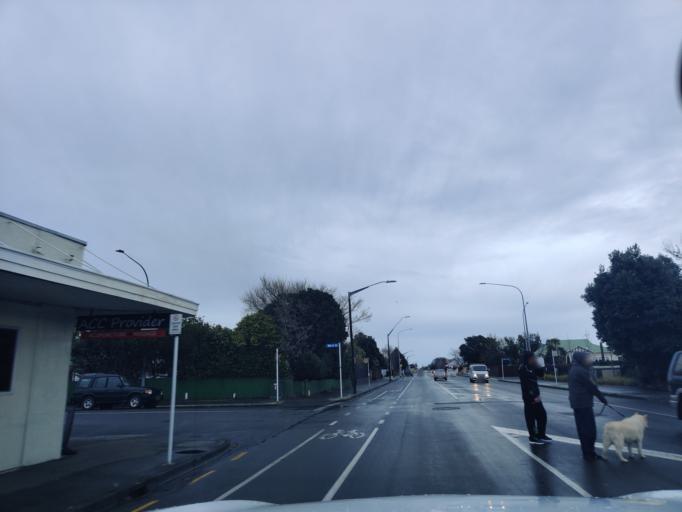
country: NZ
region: Manawatu-Wanganui
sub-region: Palmerston North City
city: Palmerston North
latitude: -40.3467
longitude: 175.6133
